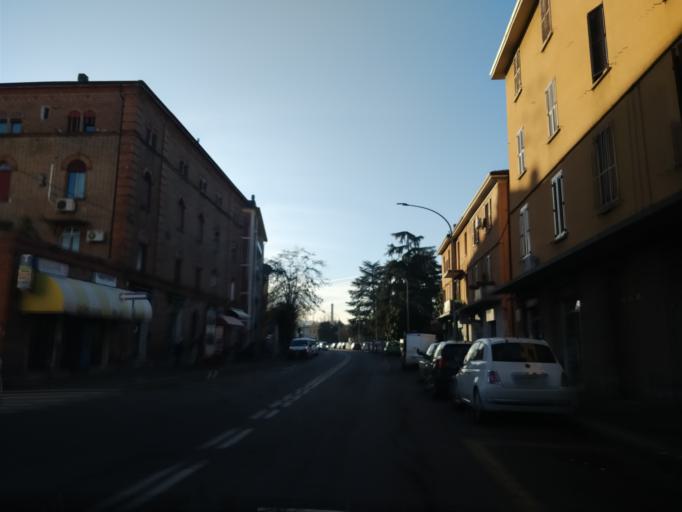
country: IT
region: Emilia-Romagna
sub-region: Provincia di Bologna
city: Bologna
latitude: 44.5167
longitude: 11.3248
